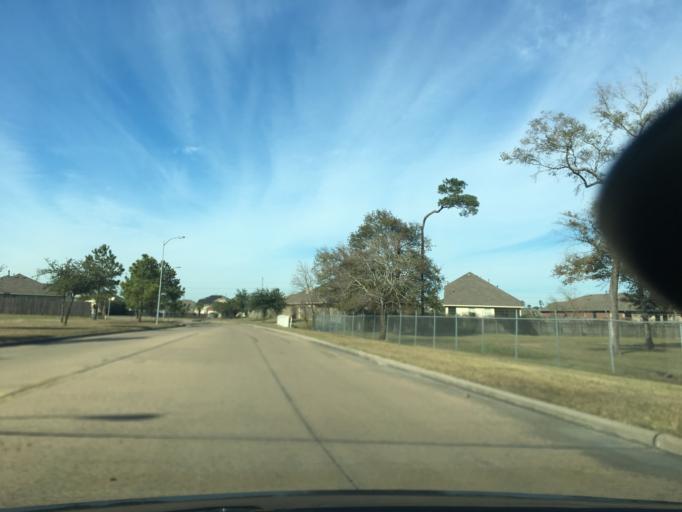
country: US
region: Texas
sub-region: Harris County
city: Cloverleaf
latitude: 29.8110
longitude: -95.1576
